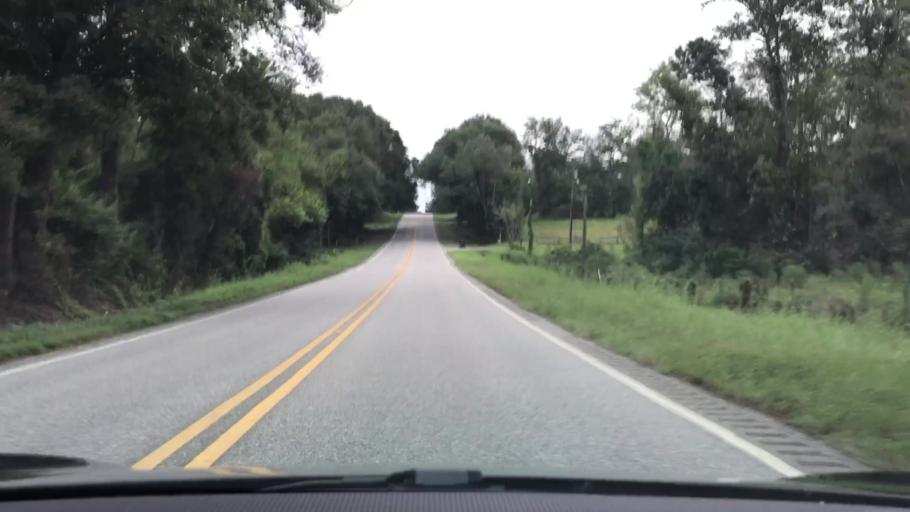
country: US
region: Alabama
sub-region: Geneva County
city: Samson
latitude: 31.0277
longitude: -86.1135
